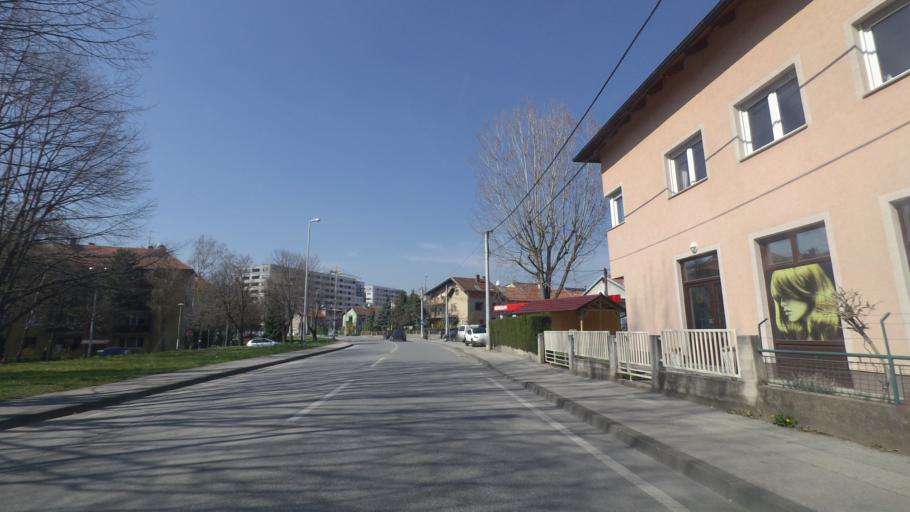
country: HR
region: Grad Zagreb
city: Zagreb
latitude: 45.8108
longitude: 16.0211
